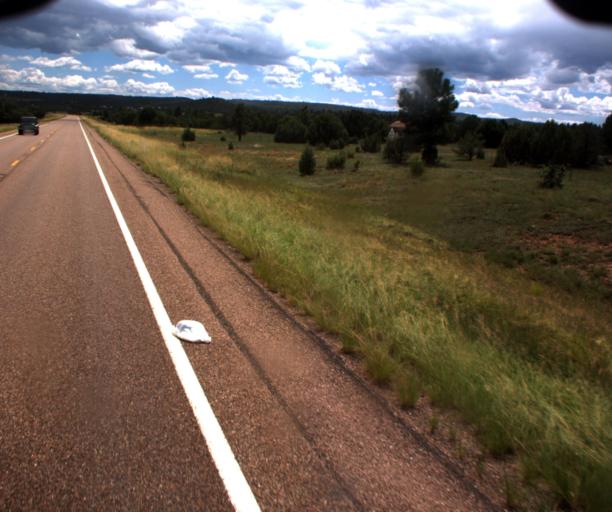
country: US
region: Arizona
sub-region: Navajo County
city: Linden
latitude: 34.3557
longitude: -110.3171
